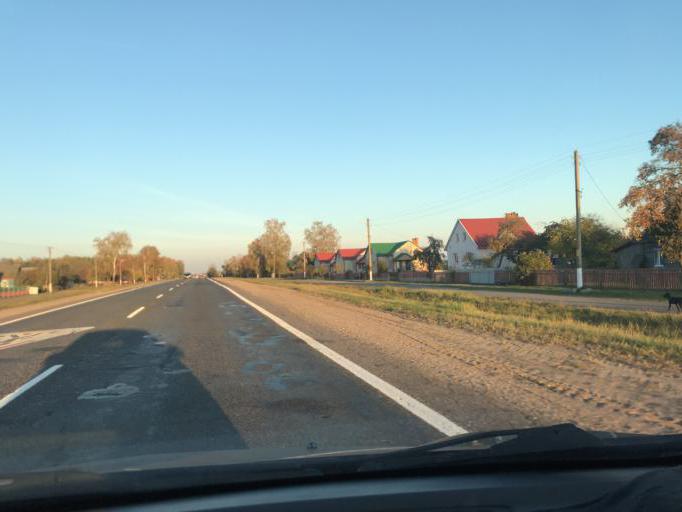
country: BY
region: Minsk
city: Staryya Darohi
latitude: 53.0503
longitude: 28.3839
